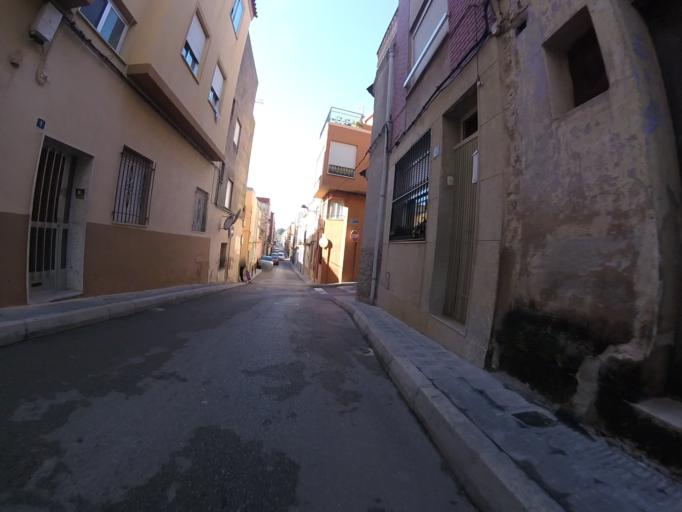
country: ES
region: Valencia
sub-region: Provincia de Castello
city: Torreblanca
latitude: 40.2210
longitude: 0.1944
